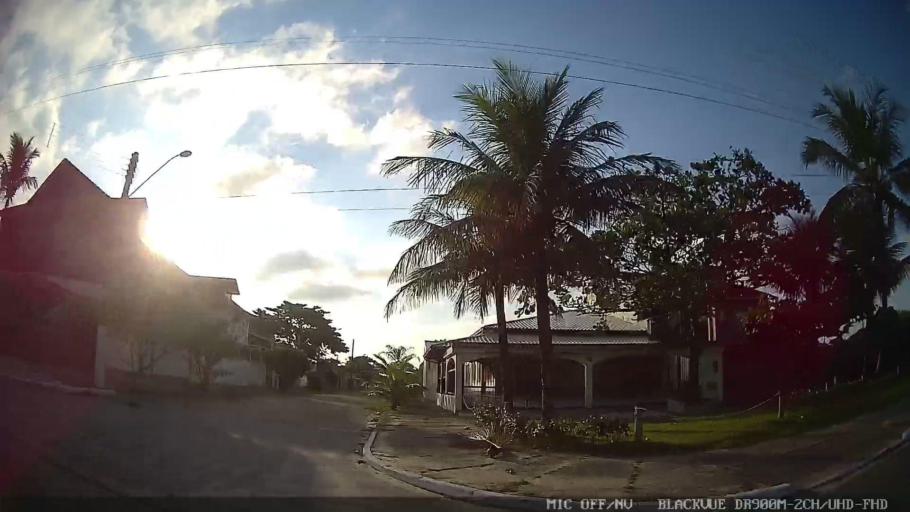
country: BR
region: Sao Paulo
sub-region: Peruibe
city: Peruibe
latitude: -24.3163
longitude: -46.9868
